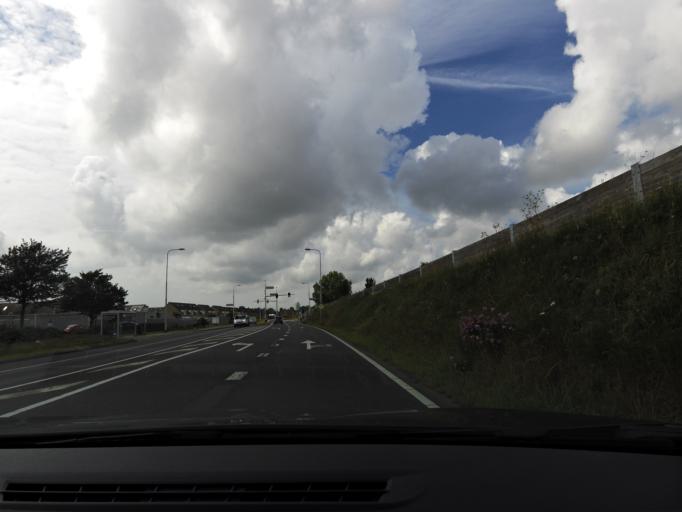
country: NL
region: Zeeland
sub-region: Gemeente Vlissingen
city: Vlissingen
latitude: 51.4618
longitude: 3.5690
